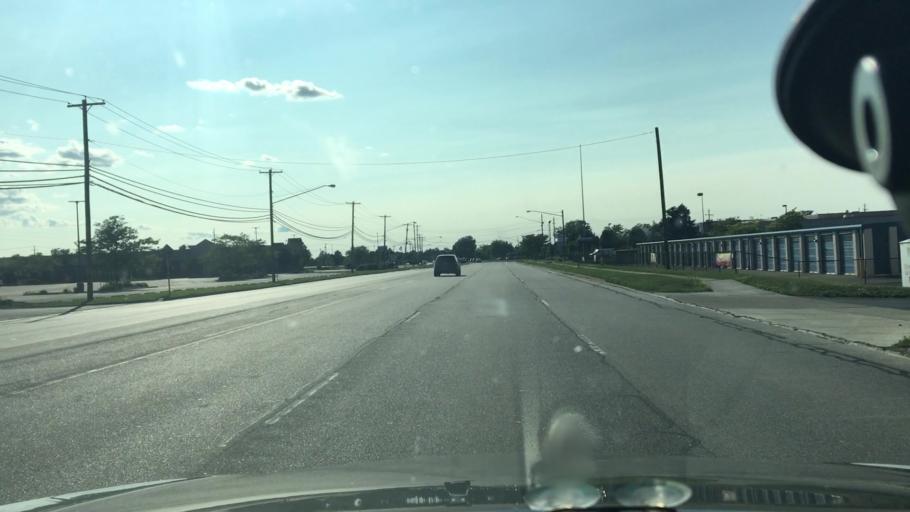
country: US
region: New York
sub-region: Erie County
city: Cheektowaga
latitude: 42.9091
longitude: -78.7247
